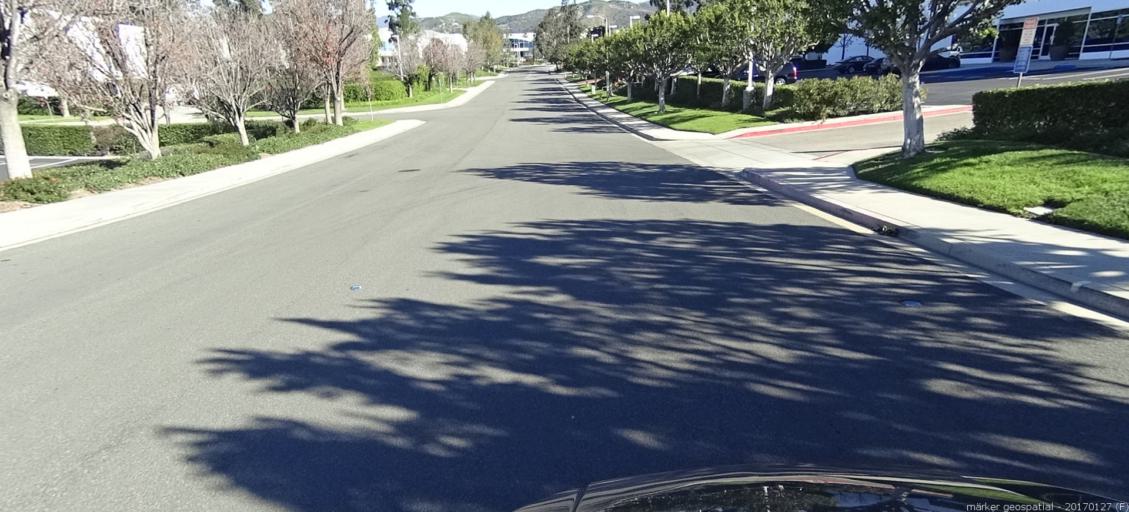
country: US
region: California
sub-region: Orange County
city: Foothill Ranch
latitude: 33.6669
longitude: -117.6599
